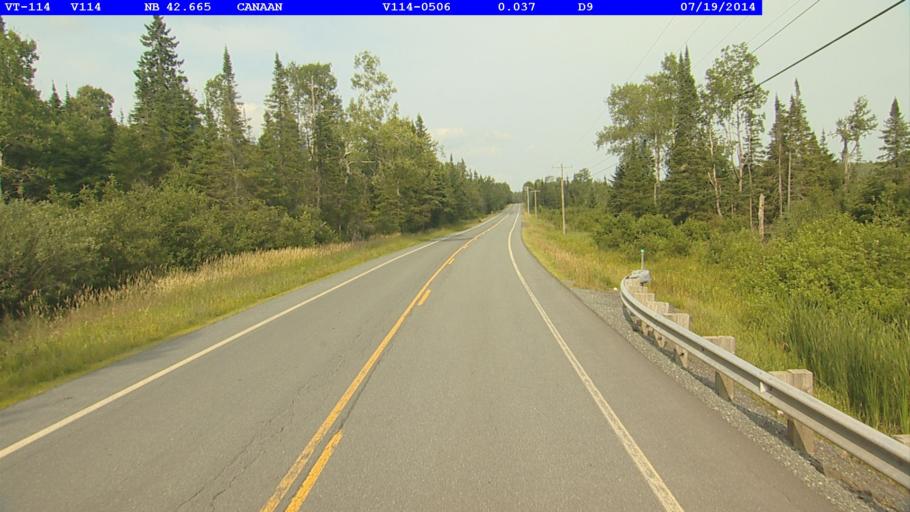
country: CA
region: Quebec
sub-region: Estrie
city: Coaticook
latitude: 45.0039
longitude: -71.6925
